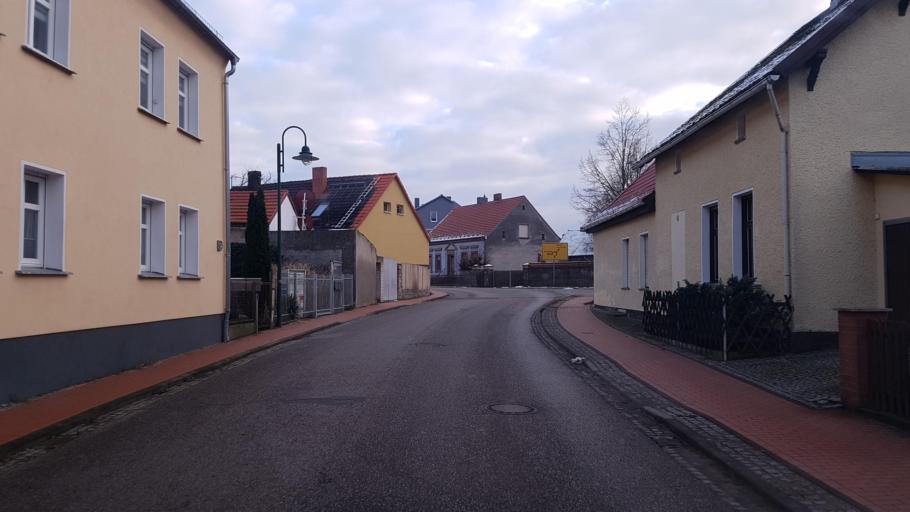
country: DE
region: Brandenburg
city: Rehfelde
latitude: 52.5079
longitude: 13.8453
